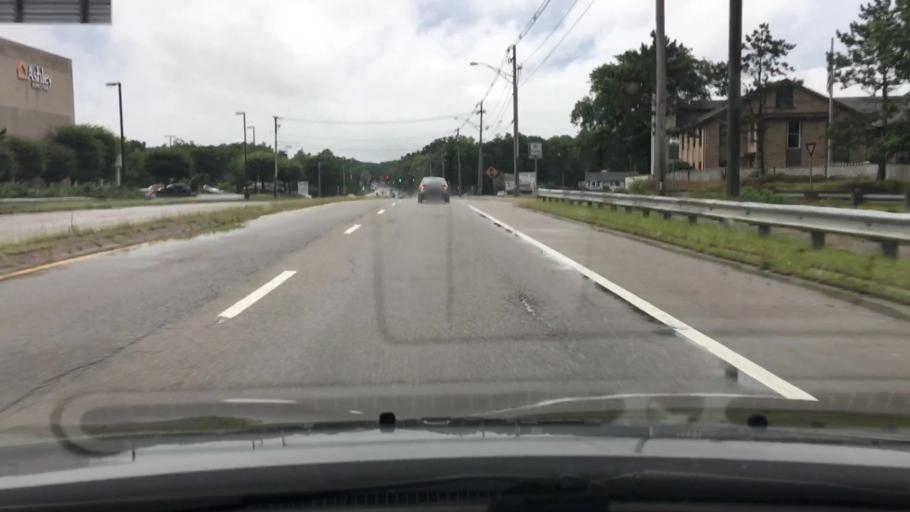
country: US
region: Massachusetts
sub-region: Bristol County
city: North Seekonk
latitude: 41.9048
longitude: -71.3564
